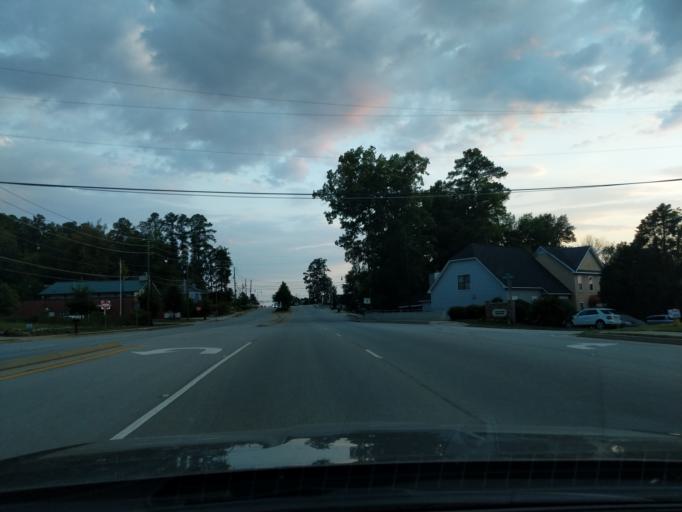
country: US
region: Georgia
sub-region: Columbia County
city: Martinez
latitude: 33.5151
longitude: -82.0259
